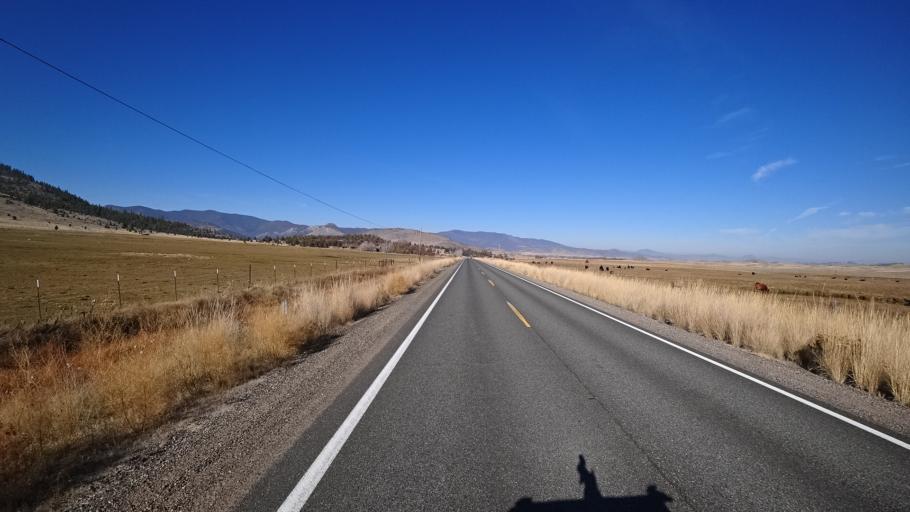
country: US
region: California
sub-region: Siskiyou County
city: Weed
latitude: 41.4881
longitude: -122.5035
